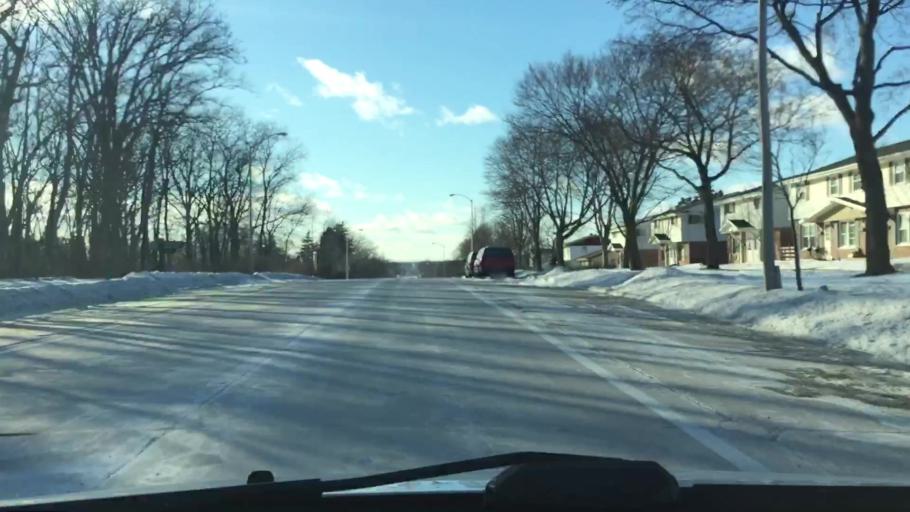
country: US
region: Wisconsin
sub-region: Milwaukee County
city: Greenfield
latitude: 42.9738
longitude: -88.0204
